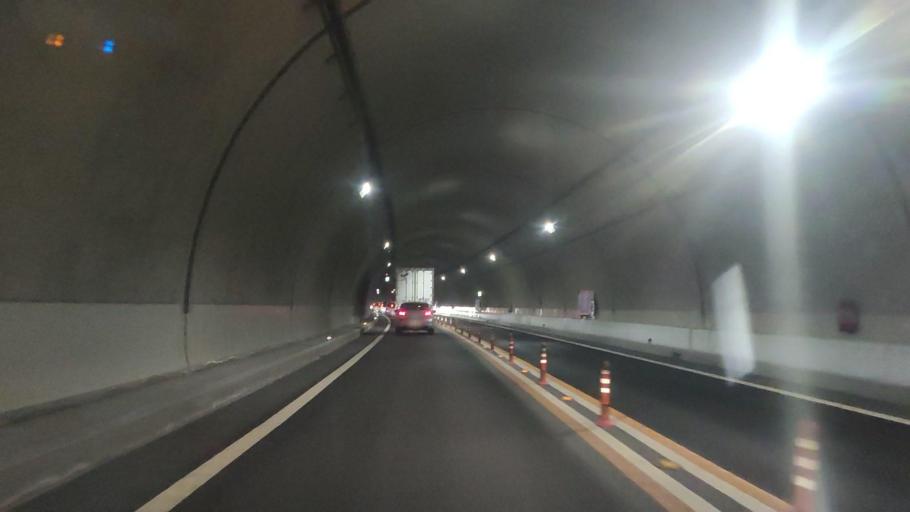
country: JP
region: Fukuoka
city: Kanda
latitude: 33.7854
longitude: 130.9717
